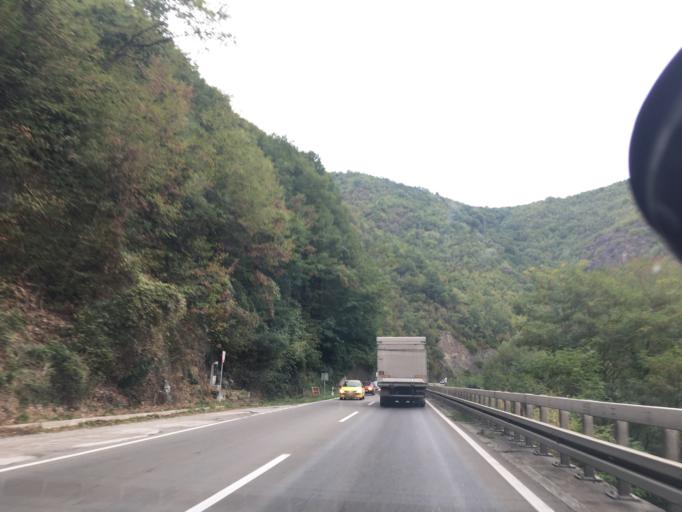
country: RS
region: Central Serbia
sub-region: Moravicki Okrug
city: Lucani
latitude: 43.9065
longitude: 20.2360
